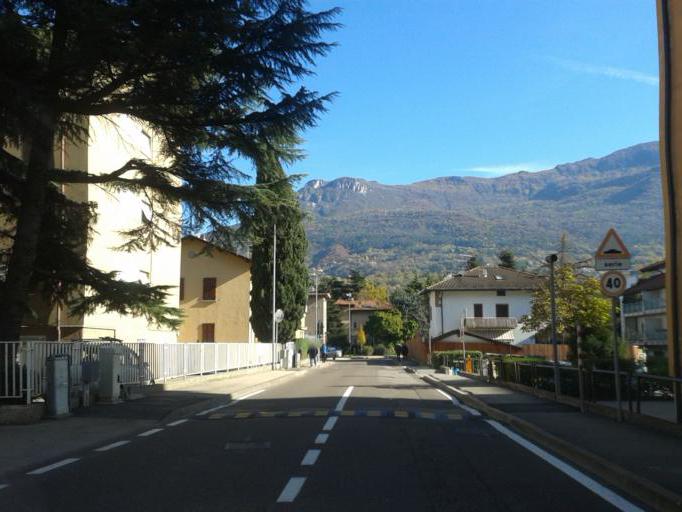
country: IT
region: Trentino-Alto Adige
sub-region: Provincia di Trento
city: Trento
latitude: 46.0525
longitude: 11.1245
